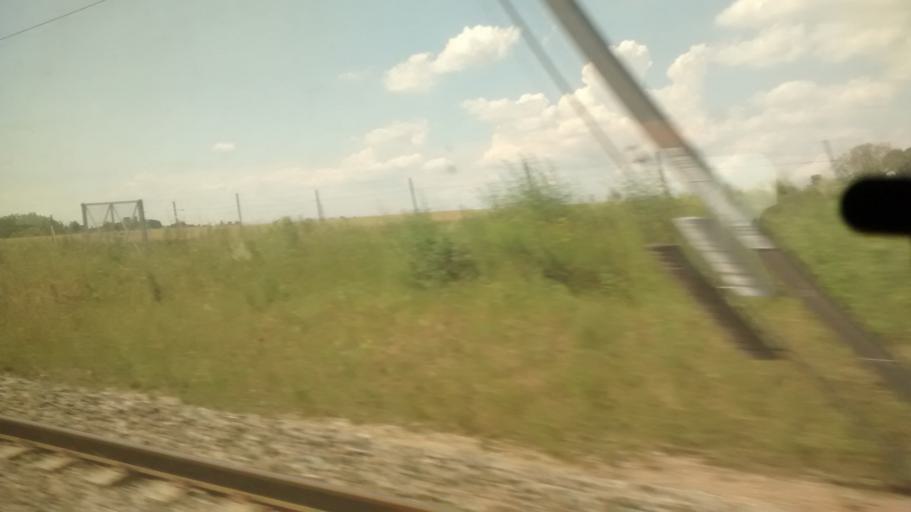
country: FR
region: Rhone-Alpes
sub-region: Departement de l'Ain
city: Grieges
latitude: 46.2118
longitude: 4.8574
